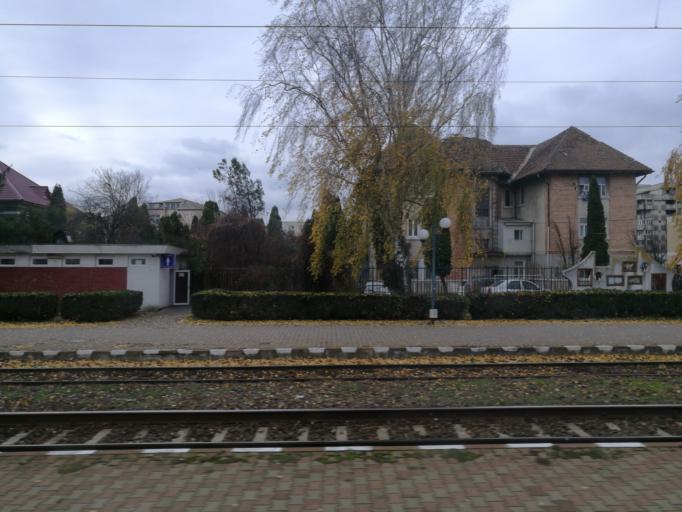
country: RO
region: Iasi
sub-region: Municipiul Pascani
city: Pascani
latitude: 47.2559
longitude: 26.7249
